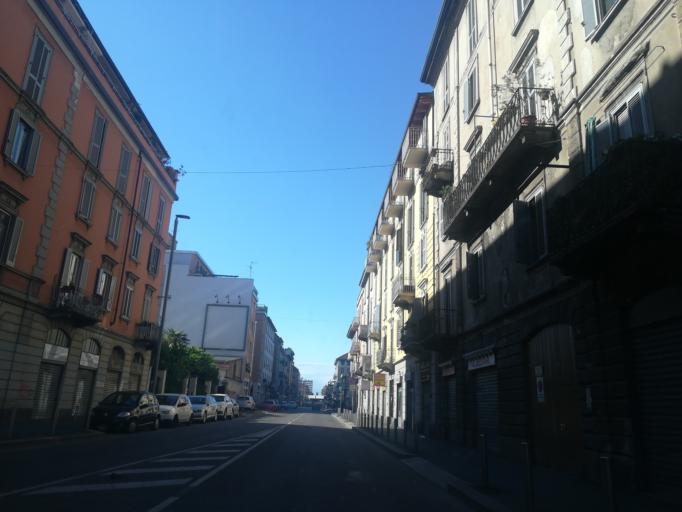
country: IT
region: Lombardy
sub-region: Citta metropolitana di Milano
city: Bresso
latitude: 45.5029
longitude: 9.1814
